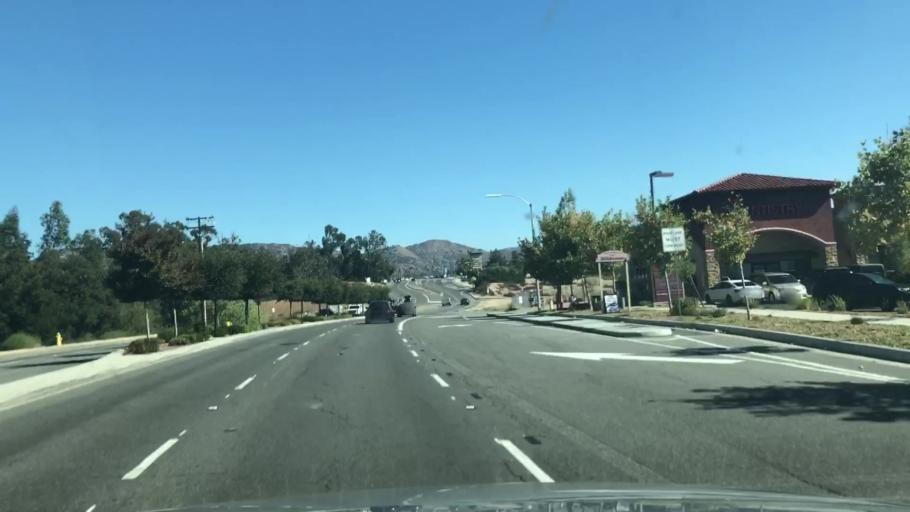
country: US
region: California
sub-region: Riverside County
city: Wildomar
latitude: 33.5916
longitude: -117.2506
